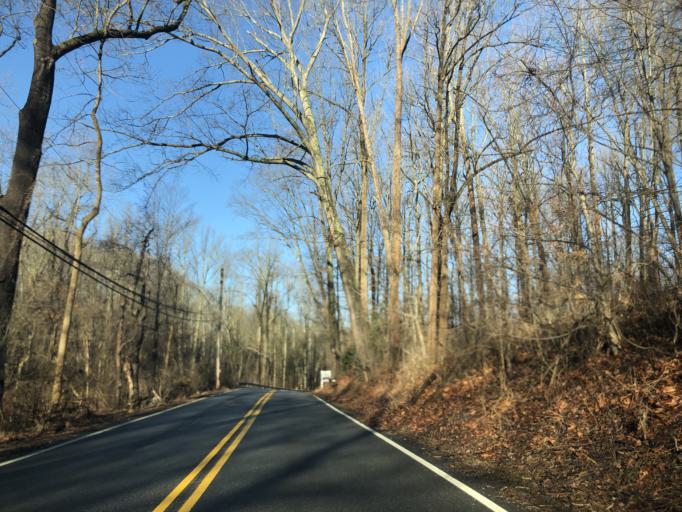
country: US
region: Pennsylvania
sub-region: Delaware County
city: Chester Heights
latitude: 39.9278
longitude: -75.4937
